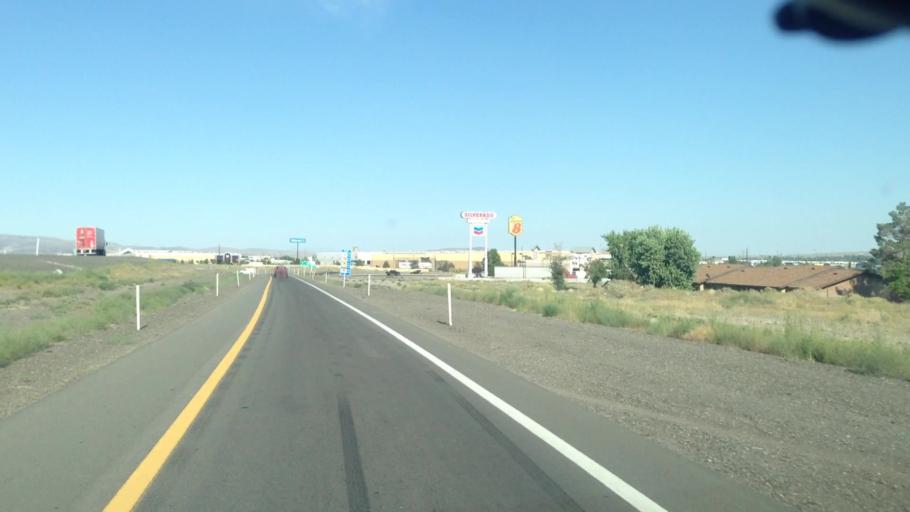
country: US
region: Nevada
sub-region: Lyon County
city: Fernley
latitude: 39.6126
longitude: -119.2229
